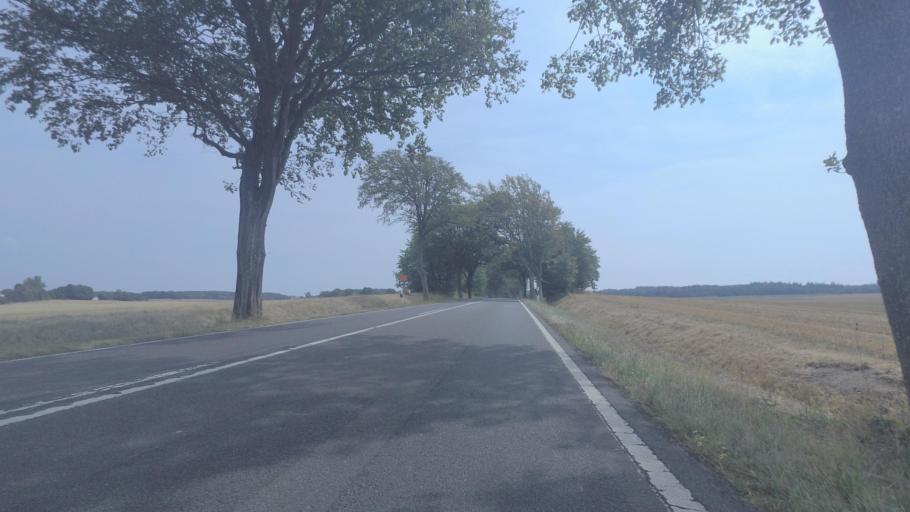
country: DE
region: Mecklenburg-Vorpommern
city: Samtens
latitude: 54.3420
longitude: 13.3107
